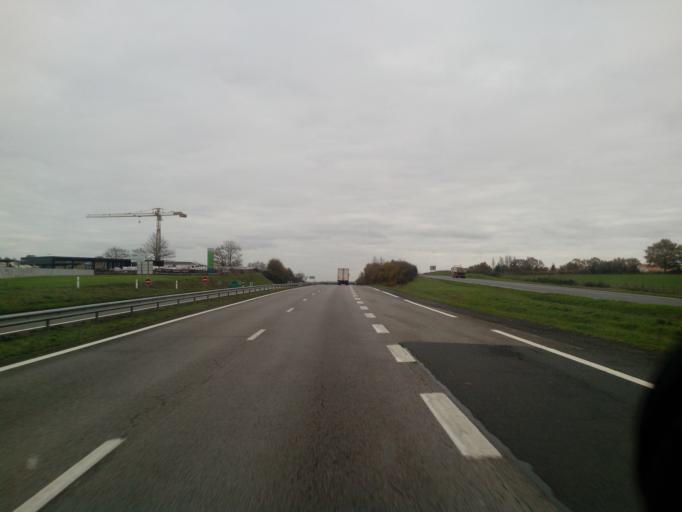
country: FR
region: Pays de la Loire
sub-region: Departement de Maine-et-Loire
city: La Seguiniere
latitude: 47.0736
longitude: -0.9419
